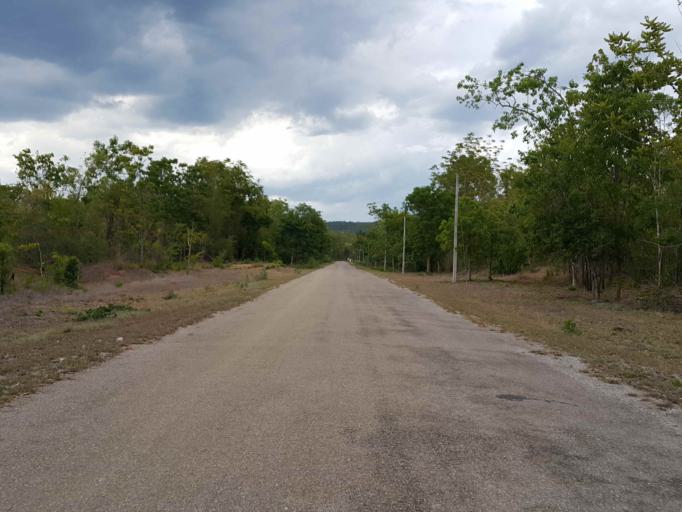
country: TH
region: Sukhothai
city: Thung Saliam
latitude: 17.3453
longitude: 99.4238
